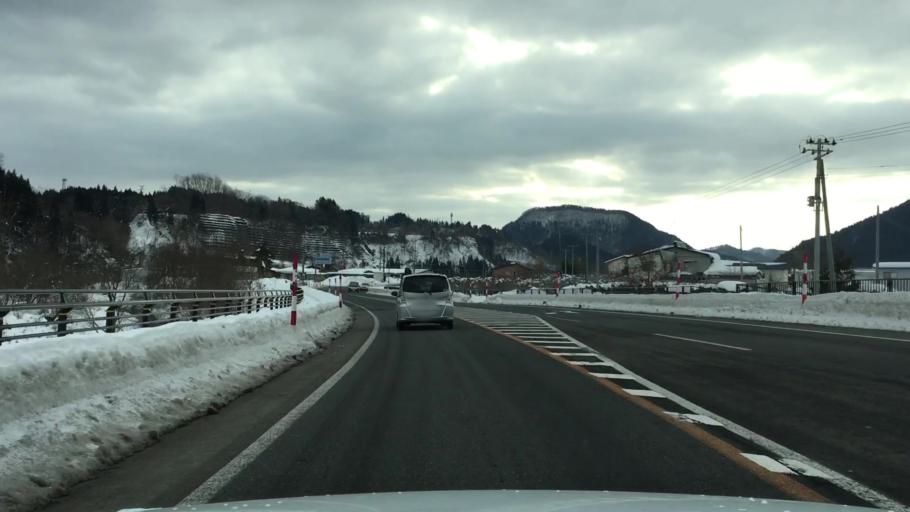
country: JP
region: Aomori
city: Kuroishi
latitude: 40.4874
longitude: 140.6211
